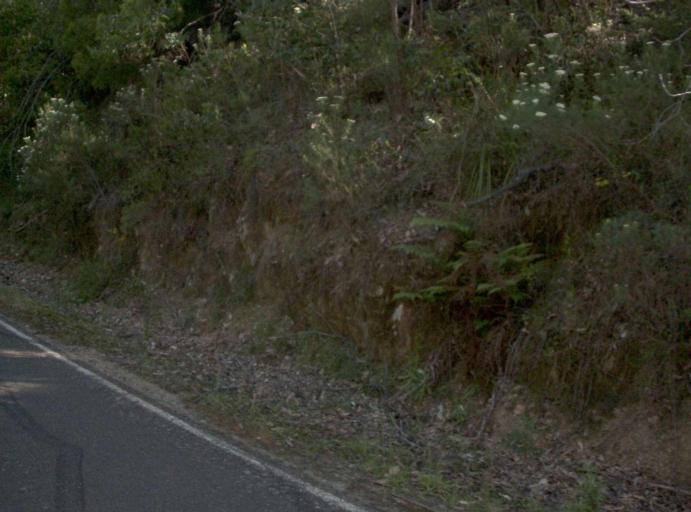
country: AU
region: Victoria
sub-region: East Gippsland
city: Lakes Entrance
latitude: -37.6445
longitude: 148.4810
